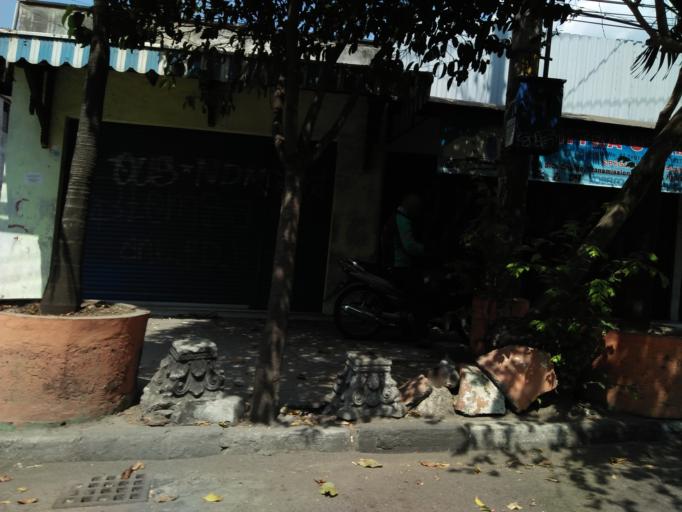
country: ID
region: Daerah Istimewa Yogyakarta
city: Kasihan
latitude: -7.8153
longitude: 110.3560
